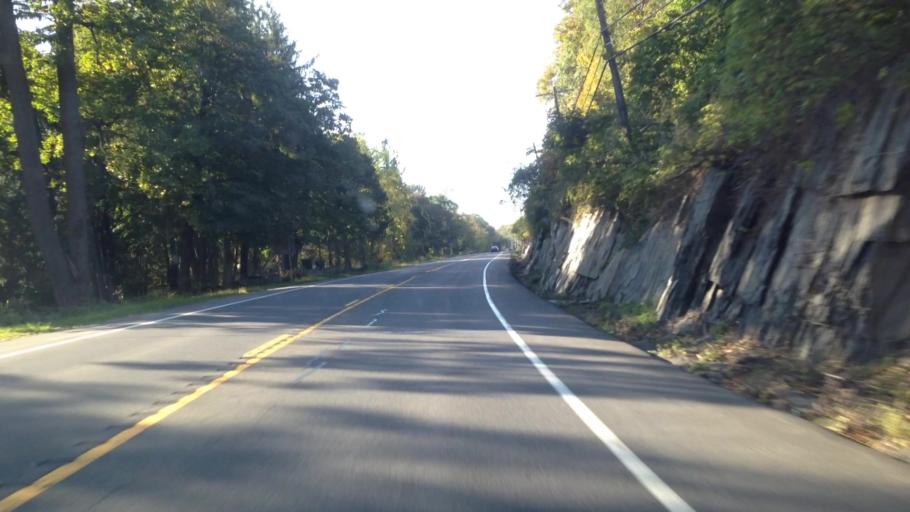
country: US
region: New York
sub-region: Dutchess County
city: Hyde Park
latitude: 41.7847
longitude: -73.9595
